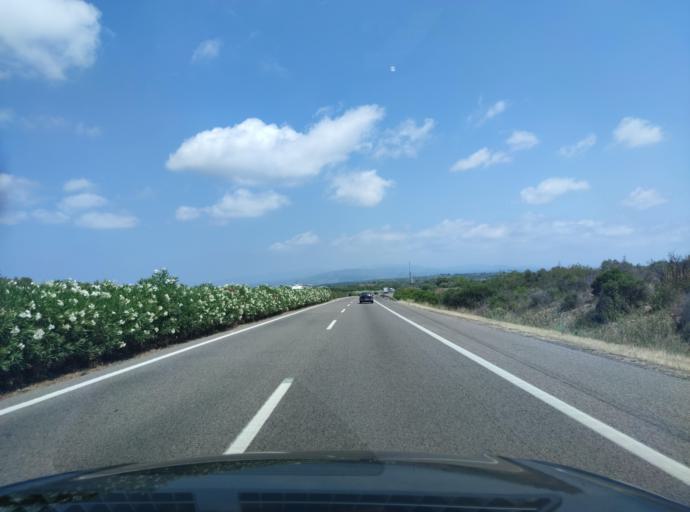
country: ES
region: Catalonia
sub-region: Provincia de Tarragona
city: Masdenverge
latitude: 40.6841
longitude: 0.5257
